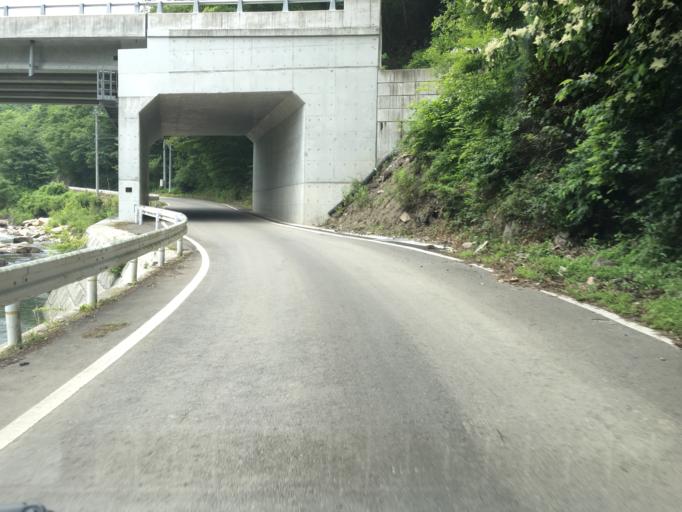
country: JP
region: Miyagi
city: Marumori
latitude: 37.7933
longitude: 140.7796
